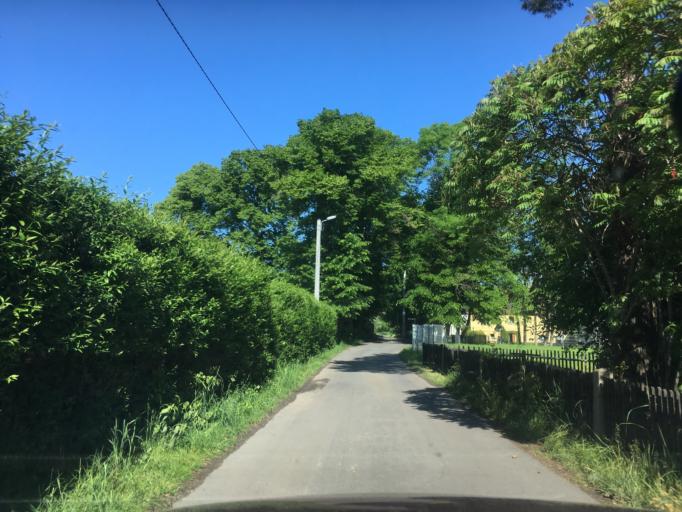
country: PL
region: Lower Silesian Voivodeship
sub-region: Powiat zgorzelecki
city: Sulikow
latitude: 51.0753
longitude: 15.0651
